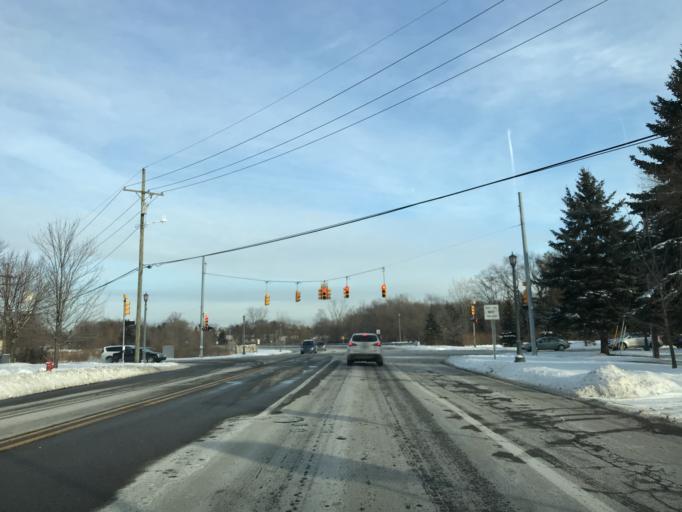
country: US
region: Michigan
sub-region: Oakland County
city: Walled Lake
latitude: 42.5329
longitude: -83.4930
